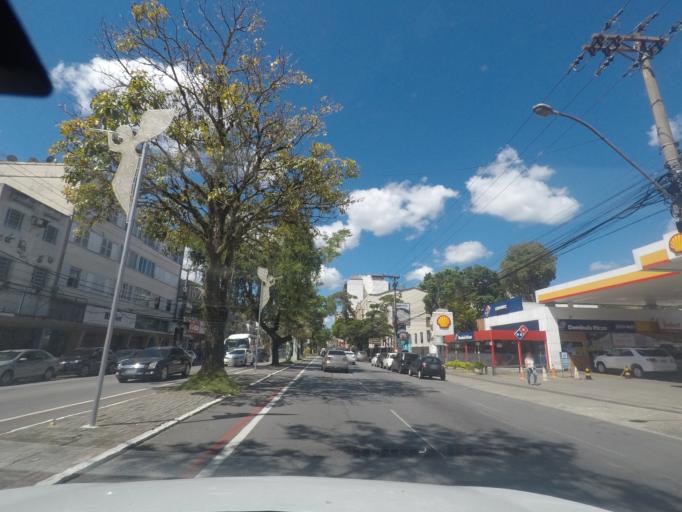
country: BR
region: Rio de Janeiro
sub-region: Teresopolis
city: Teresopolis
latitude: -22.4191
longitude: -42.9742
